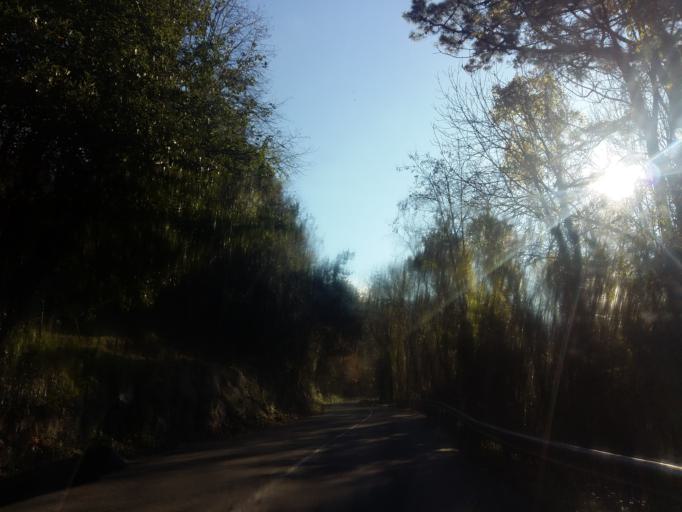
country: ES
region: Cantabria
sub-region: Provincia de Cantabria
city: Ramales de la Victoria
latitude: 43.2673
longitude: -3.4871
